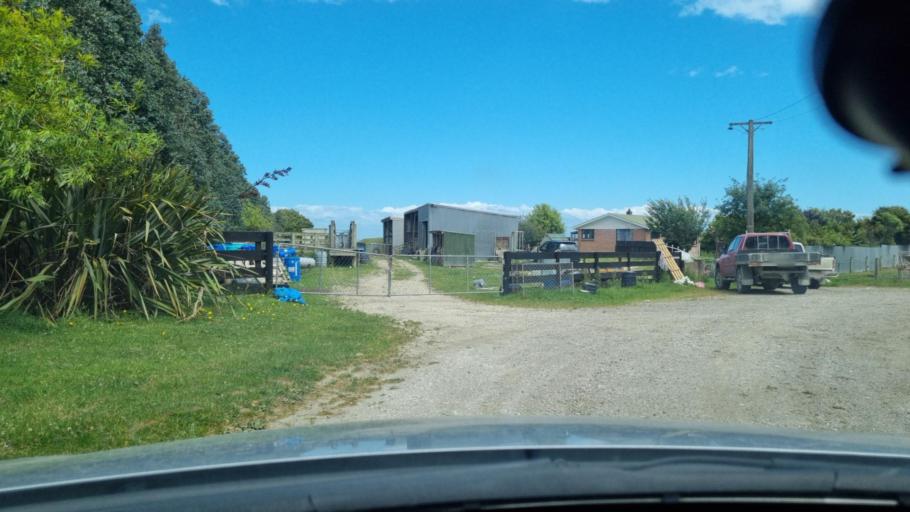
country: NZ
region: Southland
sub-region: Invercargill City
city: Invercargill
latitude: -46.4545
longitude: 168.3793
